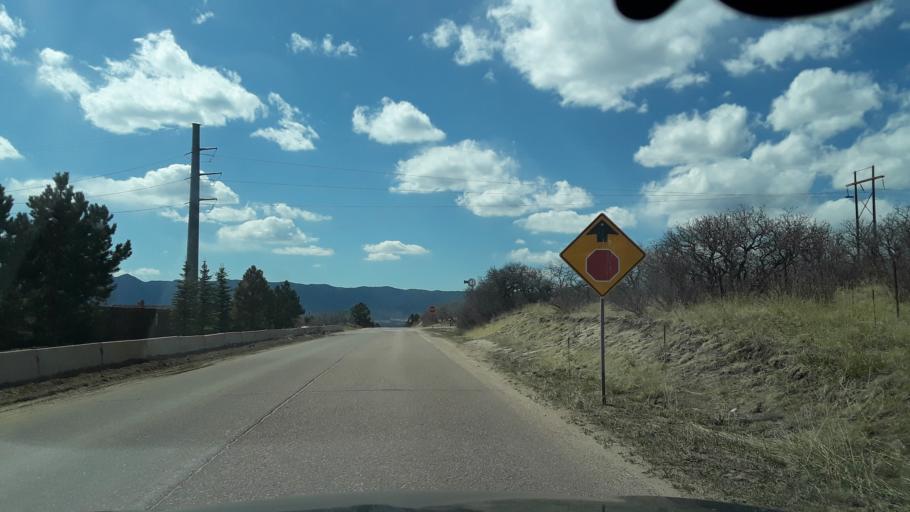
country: US
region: Colorado
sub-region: El Paso County
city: Gleneagle
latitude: 39.0347
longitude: -104.7834
